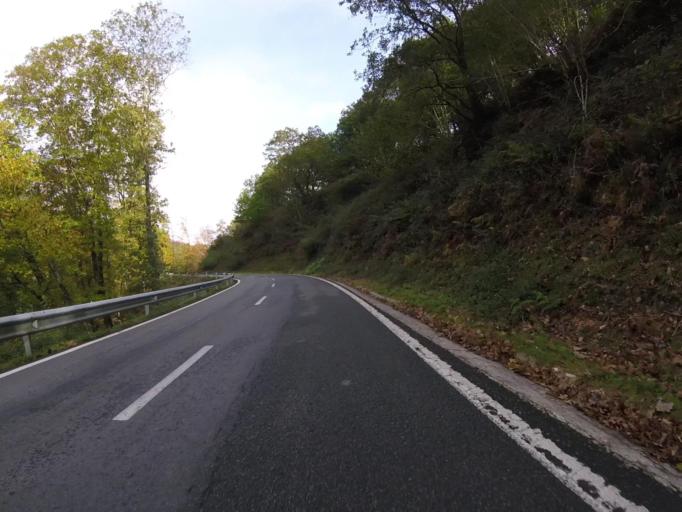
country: ES
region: Navarre
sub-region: Provincia de Navarra
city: Goizueta
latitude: 43.2026
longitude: -1.8598
